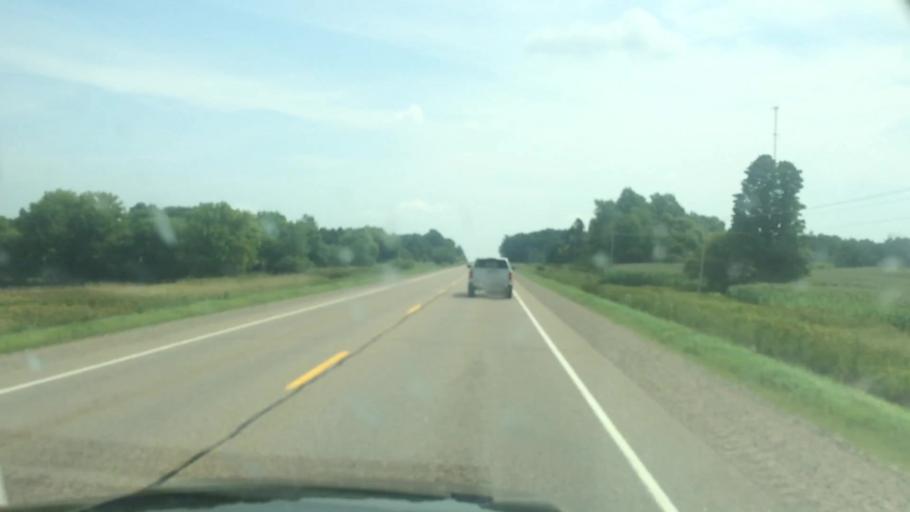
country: US
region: Wisconsin
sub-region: Langlade County
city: Antigo
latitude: 45.1681
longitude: -88.9037
